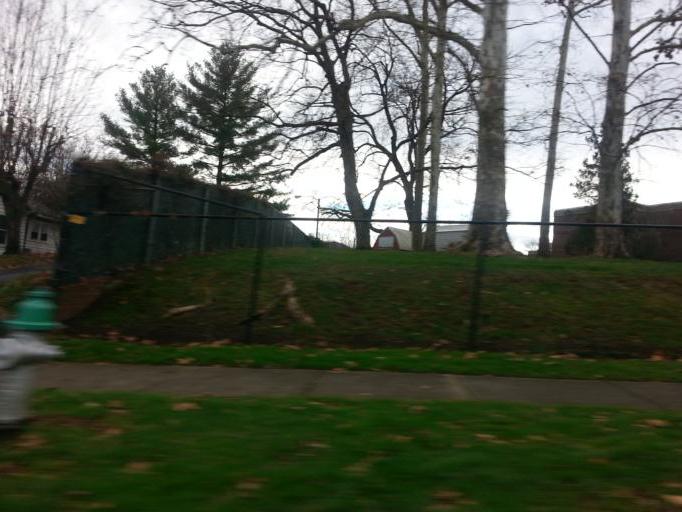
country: US
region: Tennessee
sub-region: Washington County
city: Johnson City
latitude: 36.3118
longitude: -82.3689
